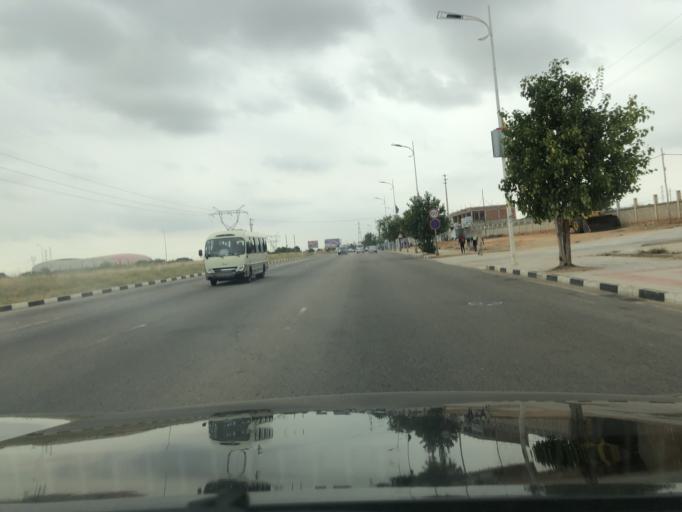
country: AO
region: Luanda
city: Luanda
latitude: -8.9820
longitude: 13.2900
